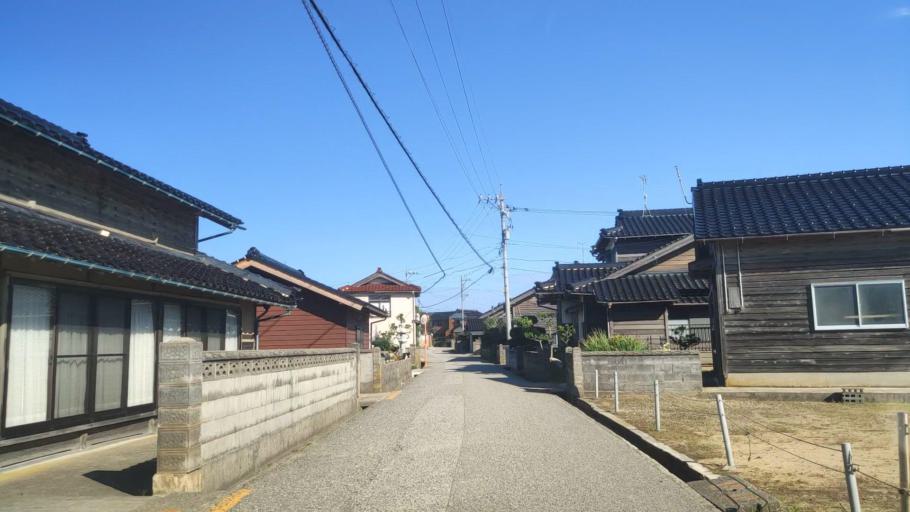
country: JP
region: Ishikawa
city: Hakui
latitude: 36.9466
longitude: 136.7632
